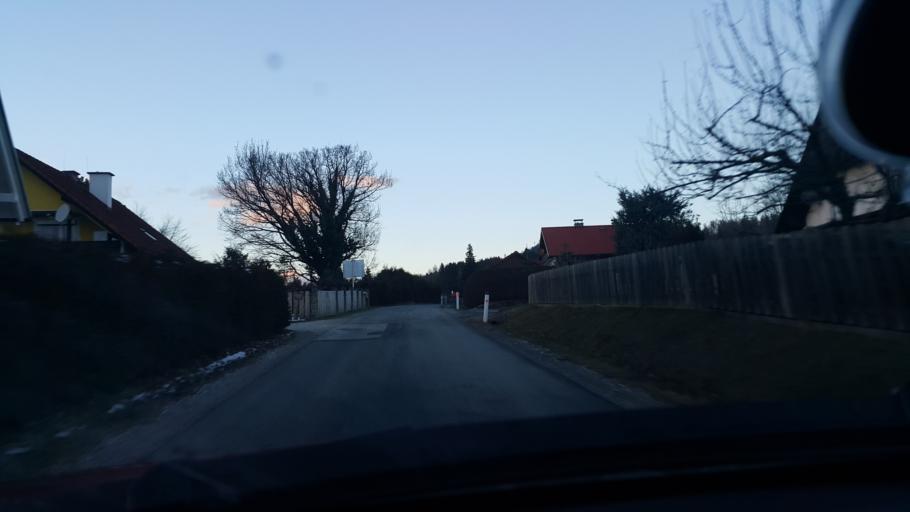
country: AT
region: Styria
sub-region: Politischer Bezirk Graz-Umgebung
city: Stiwoll
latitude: 47.1116
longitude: 15.2212
